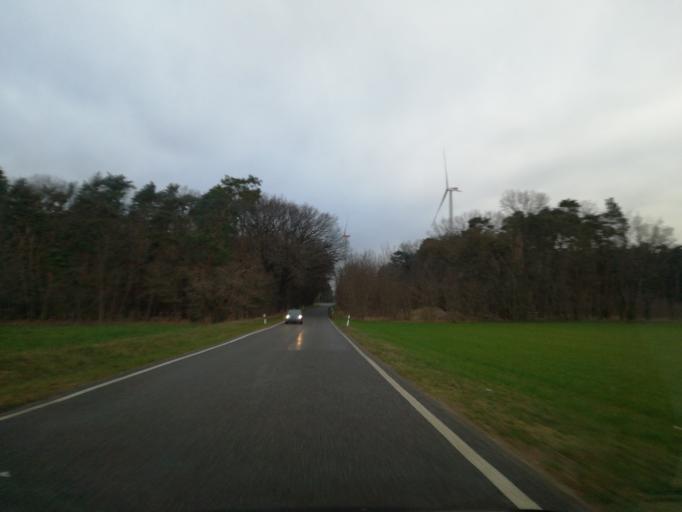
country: DE
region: Brandenburg
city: Vetschau
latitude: 51.7478
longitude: 14.0955
